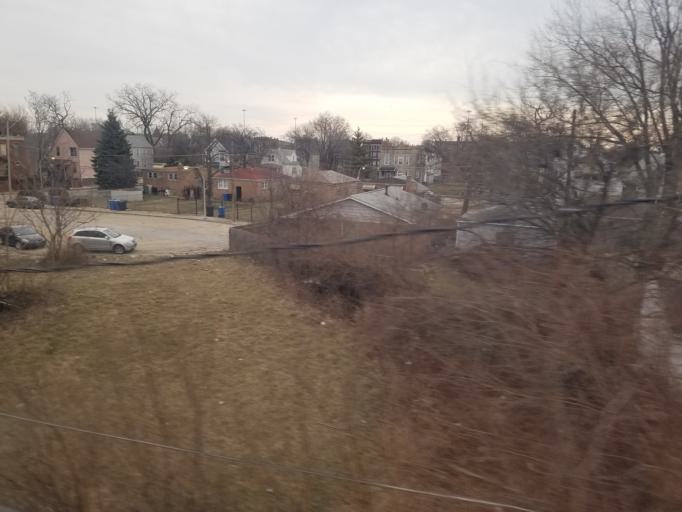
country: US
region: Illinois
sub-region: Cook County
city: Chicago
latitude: 41.7917
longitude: -87.6284
